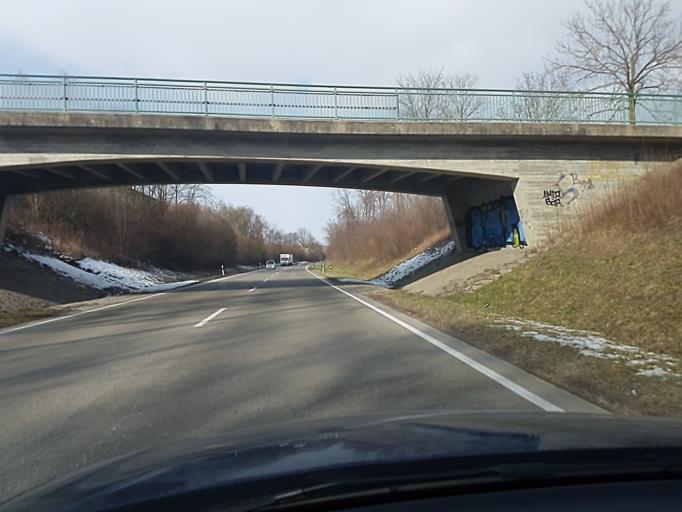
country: DE
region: Baden-Wuerttemberg
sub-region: Regierungsbezirk Stuttgart
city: Bondorf
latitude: 48.5237
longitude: 8.8443
